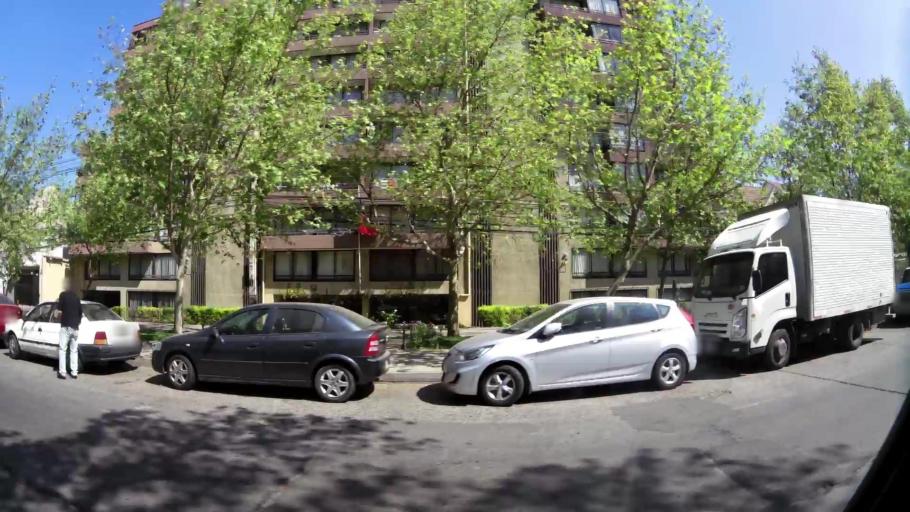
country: CL
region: Santiago Metropolitan
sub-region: Provincia de Santiago
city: Santiago
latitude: -33.4594
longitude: -70.6640
